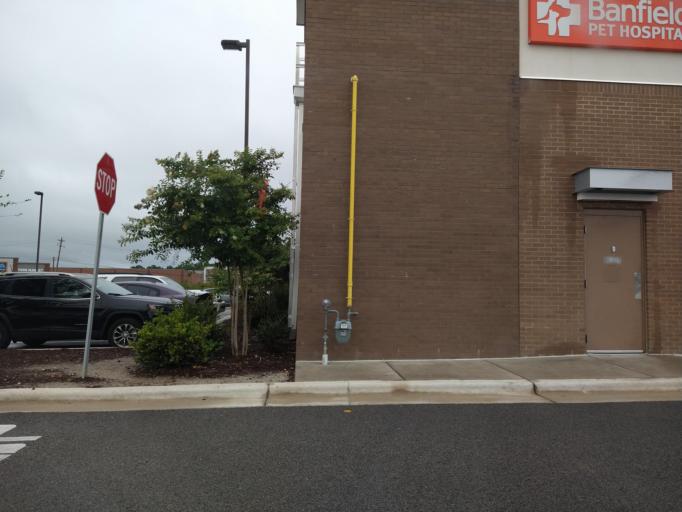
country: US
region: North Carolina
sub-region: Onslow County
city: Pumpkin Center
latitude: 34.7973
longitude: -77.4136
